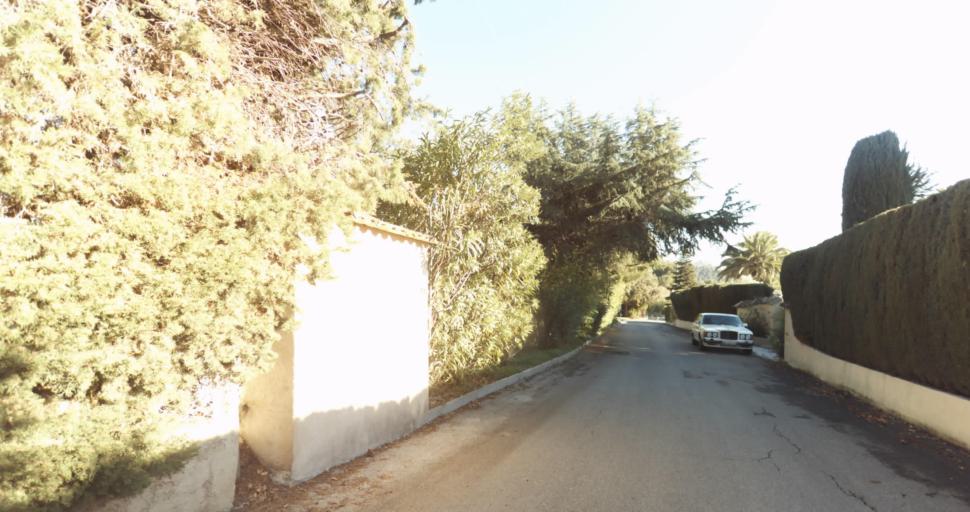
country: FR
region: Provence-Alpes-Cote d'Azur
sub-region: Departement des Alpes-Maritimes
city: Saint-Paul-de-Vence
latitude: 43.6976
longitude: 7.1365
